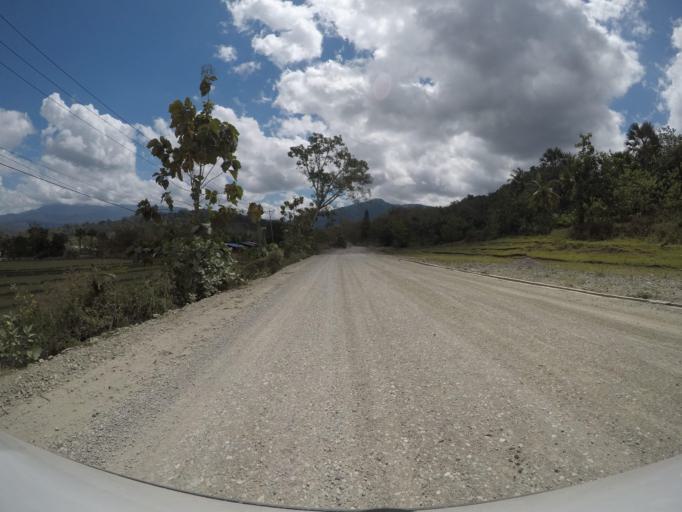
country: TL
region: Viqueque
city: Viqueque
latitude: -8.8231
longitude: 126.3779
